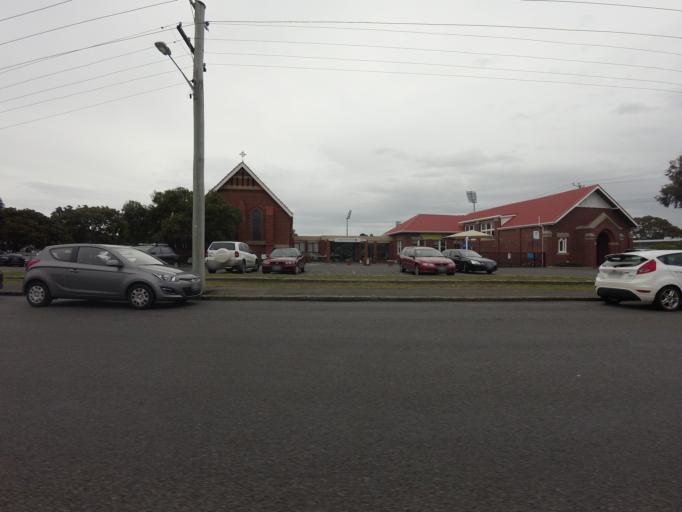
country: AU
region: Tasmania
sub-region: Clarence
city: Bellerive
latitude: -42.8751
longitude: 147.3710
